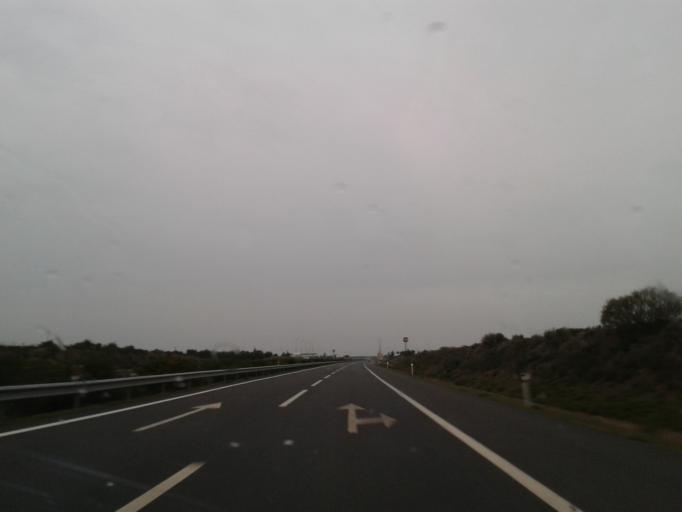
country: PT
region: Beja
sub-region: Aljustrel
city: Aljustrel
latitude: 37.9178
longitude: -8.2424
